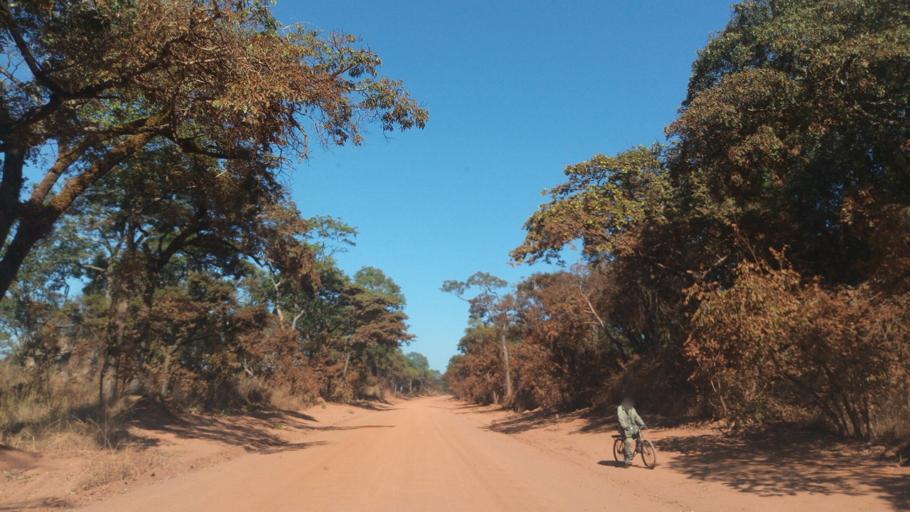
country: ZM
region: Luapula
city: Mwense
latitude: -10.7356
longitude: 28.3409
